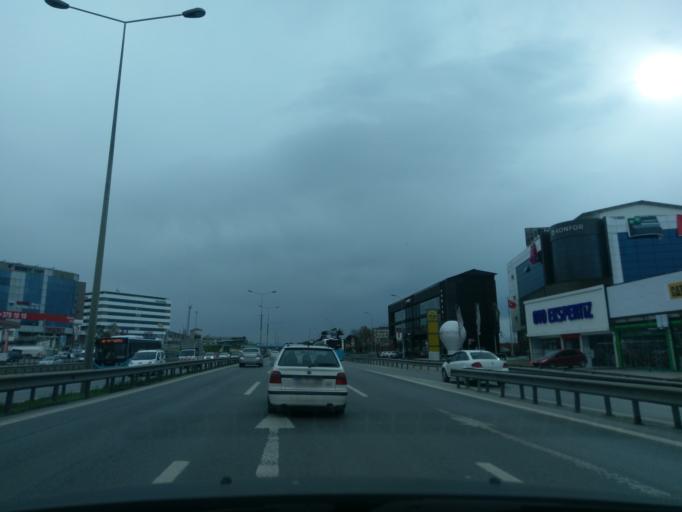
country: TR
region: Istanbul
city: Pendik
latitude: 40.8905
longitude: 29.2350
